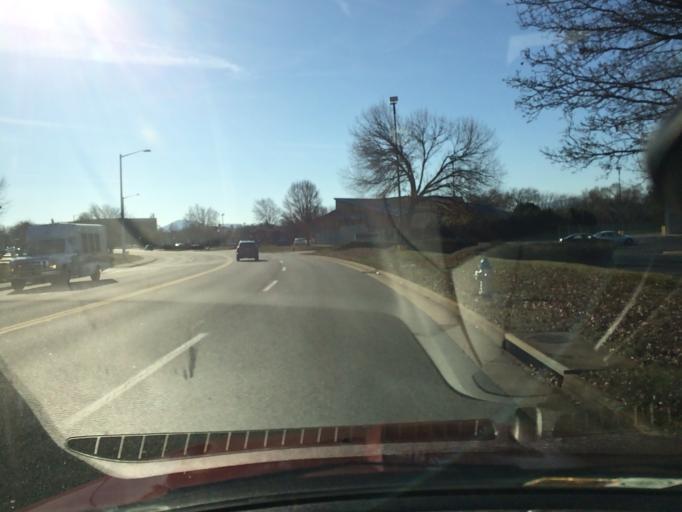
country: US
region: Virginia
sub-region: Roanoke County
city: Hollins
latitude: 37.3076
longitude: -79.9695
